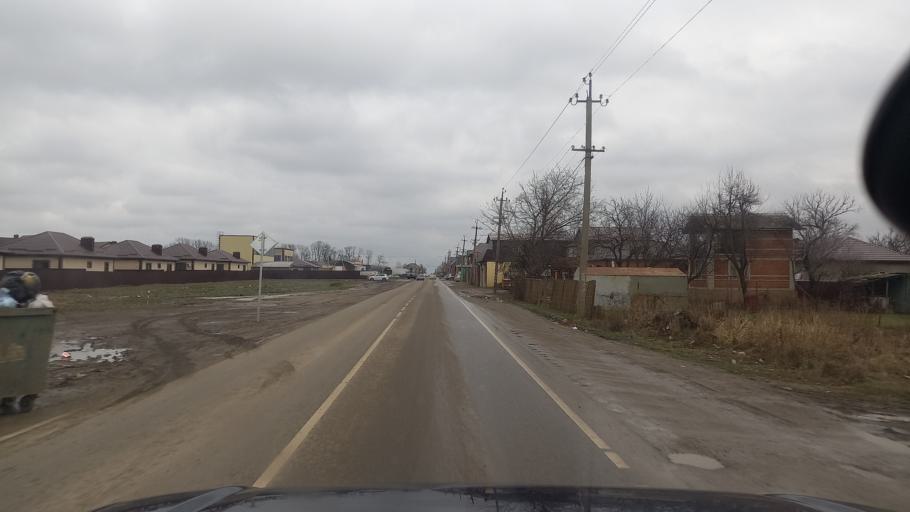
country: RU
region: Krasnodarskiy
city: Pashkovskiy
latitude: 45.0592
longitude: 39.1695
